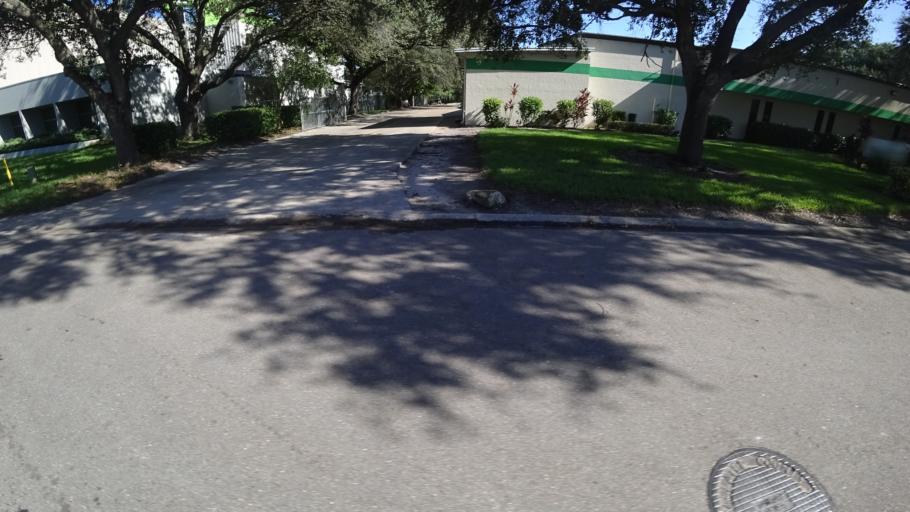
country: US
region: Florida
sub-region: Manatee County
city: Whitfield
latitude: 27.4244
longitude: -82.5344
